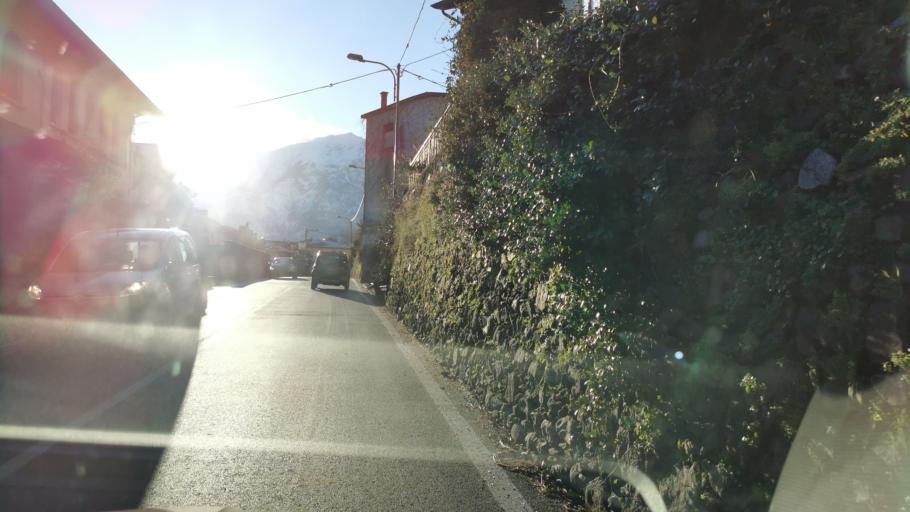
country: IT
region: Lombardy
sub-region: Provincia di Como
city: Gravedona-San Gregorio
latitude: 46.1484
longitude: 9.3040
